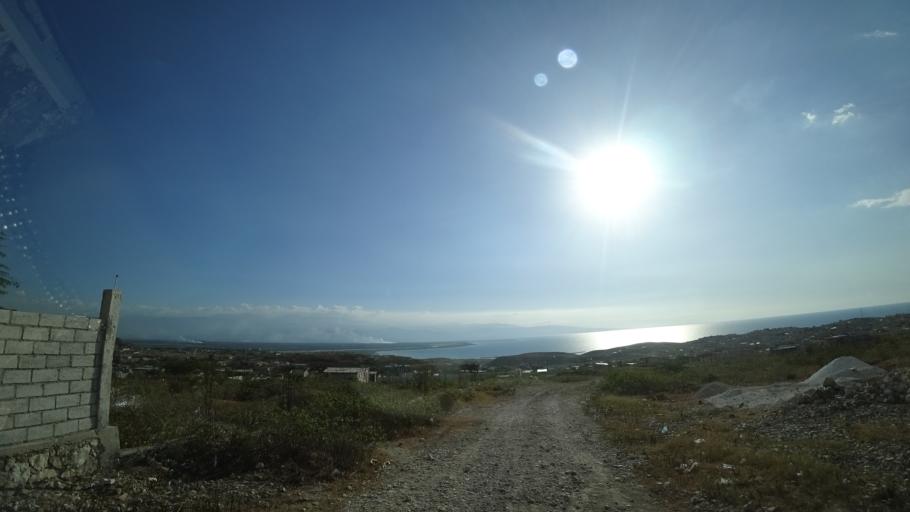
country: HT
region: Ouest
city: Cabaret
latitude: 18.6902
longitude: -72.3103
